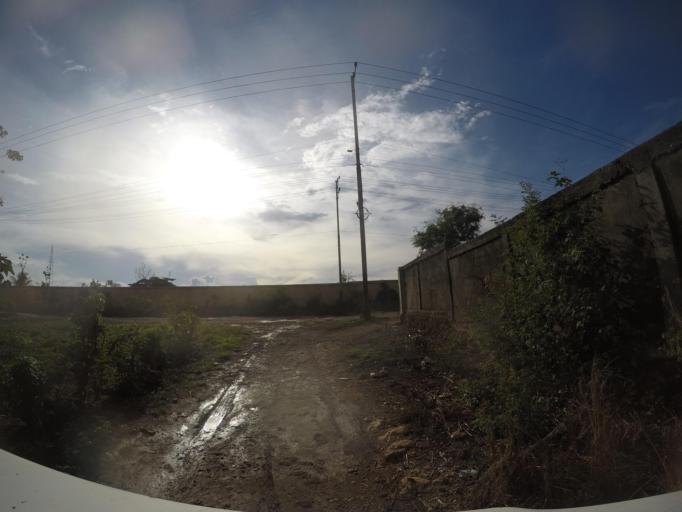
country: TL
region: Baucau
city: Baucau
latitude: -8.4854
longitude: 126.4548
